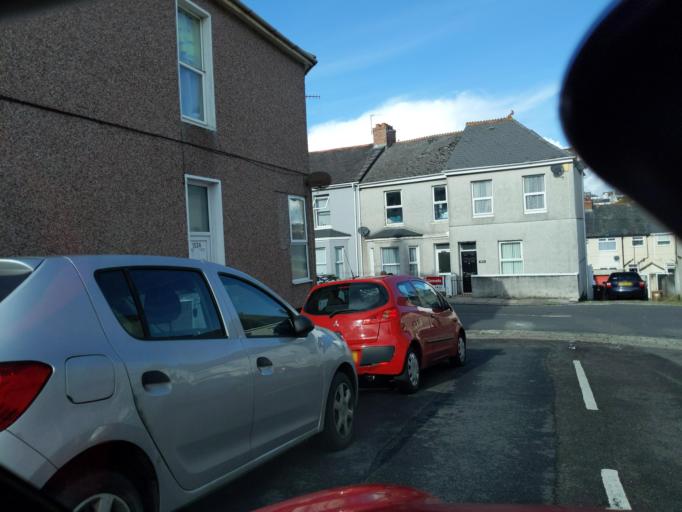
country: GB
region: England
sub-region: Plymouth
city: Plymouth
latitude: 50.3718
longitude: -4.1184
